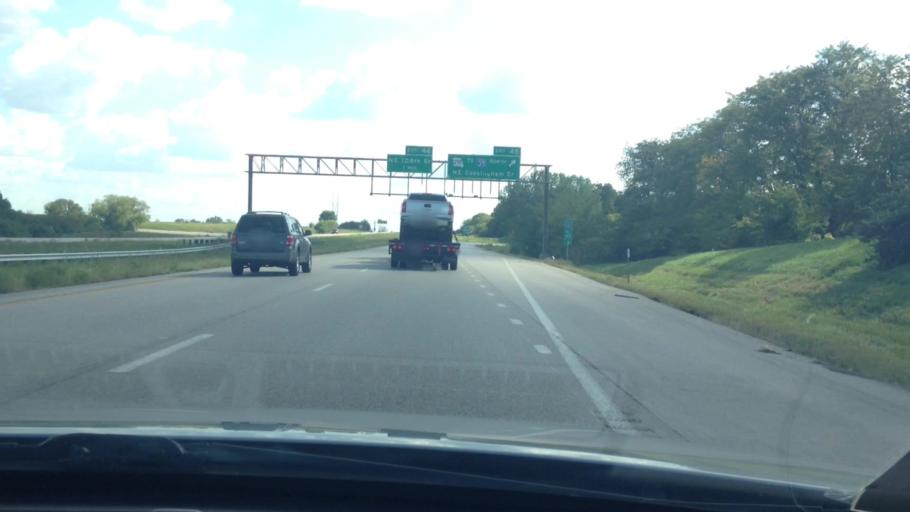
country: US
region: Missouri
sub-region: Clay County
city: Pleasant Valley
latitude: 39.3019
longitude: -94.5104
